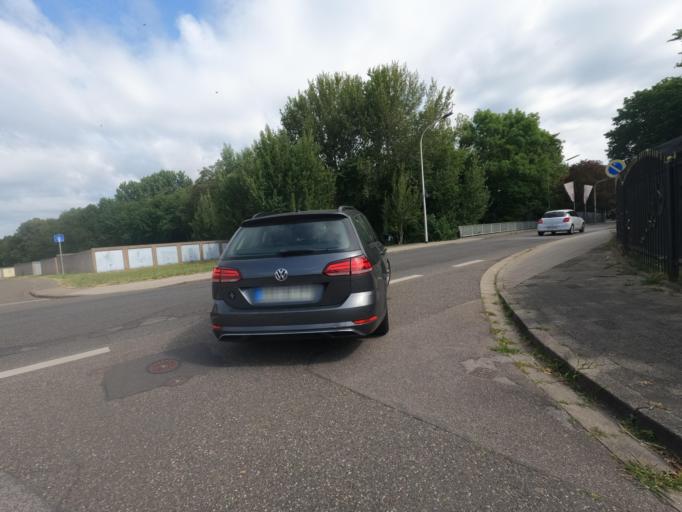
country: DE
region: North Rhine-Westphalia
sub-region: Regierungsbezirk Koln
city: Wassenberg
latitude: 51.0558
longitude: 6.1452
